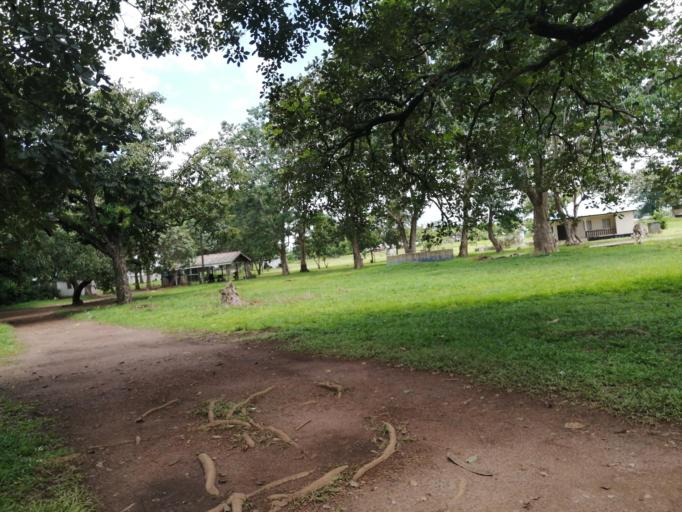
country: SL
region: Northern Province
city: Port Loko
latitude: 8.7772
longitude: -12.7925
